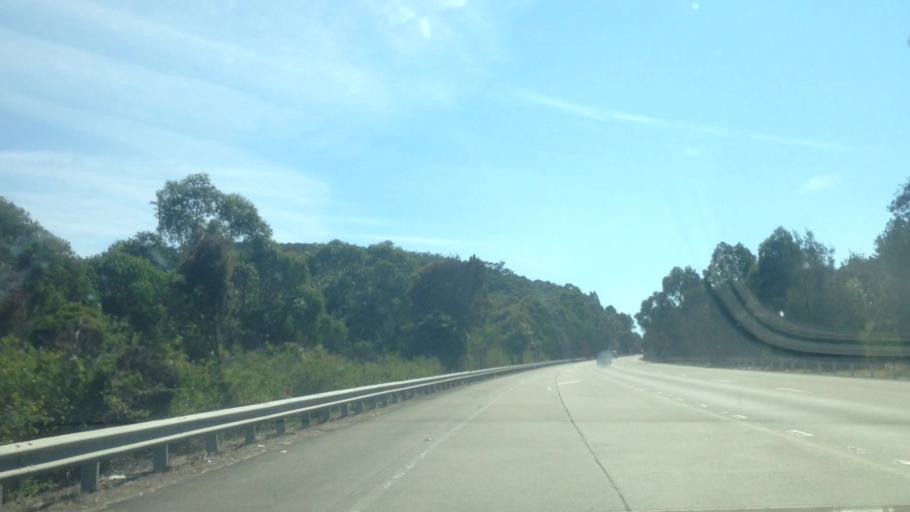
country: AU
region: New South Wales
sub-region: Lake Macquarie Shire
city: Toronto
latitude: -32.9840
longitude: 151.5214
